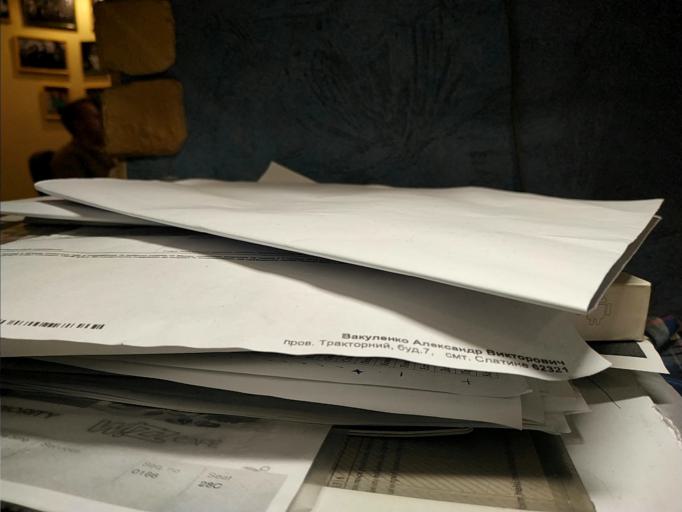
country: RU
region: Tverskaya
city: Zubtsov
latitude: 56.1241
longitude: 34.5508
